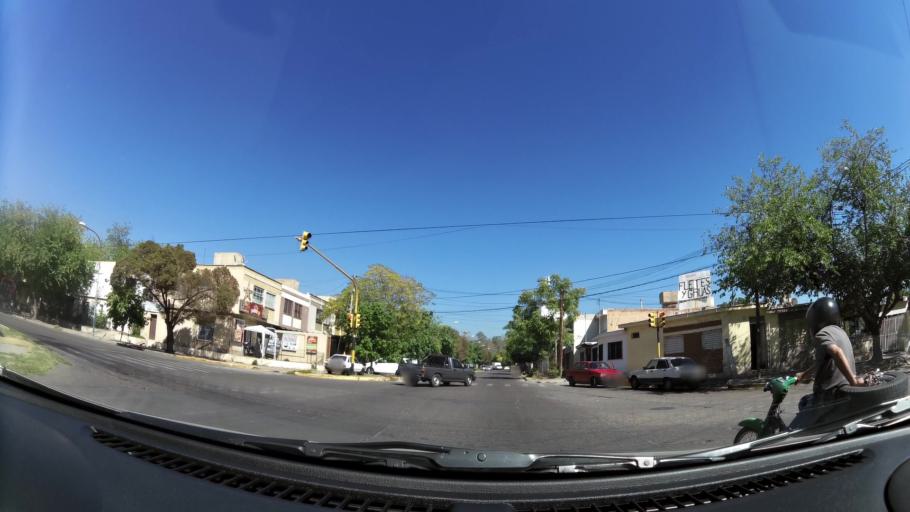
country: AR
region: Mendoza
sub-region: Departamento de Godoy Cruz
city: Godoy Cruz
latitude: -32.9076
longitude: -68.8740
